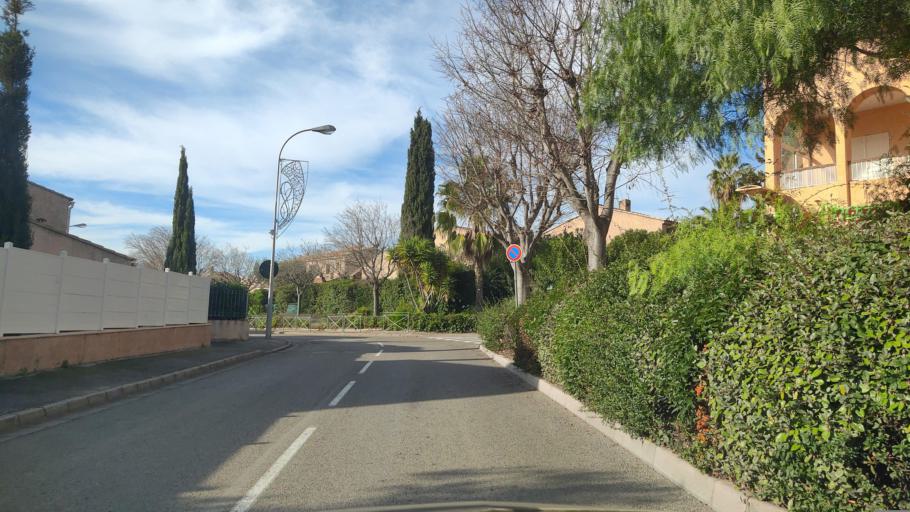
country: FR
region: Provence-Alpes-Cote d'Azur
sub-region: Departement du Var
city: Sanary-sur-Mer
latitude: 43.1275
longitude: 5.8037
